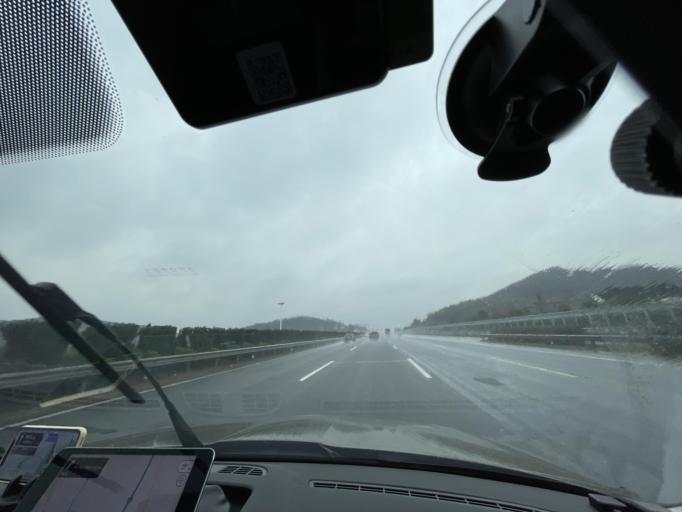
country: CN
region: Zhejiang Sheng
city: Yuanhua
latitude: 30.4001
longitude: 120.7902
